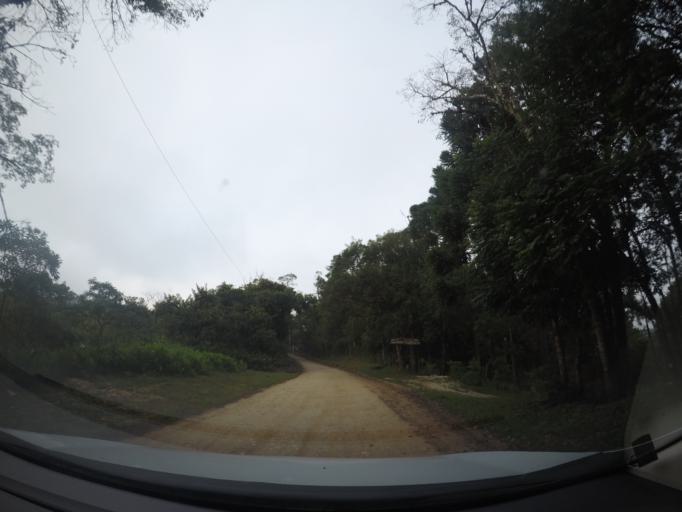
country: BR
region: Parana
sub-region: Colombo
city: Colombo
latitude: -25.3110
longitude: -49.2452
